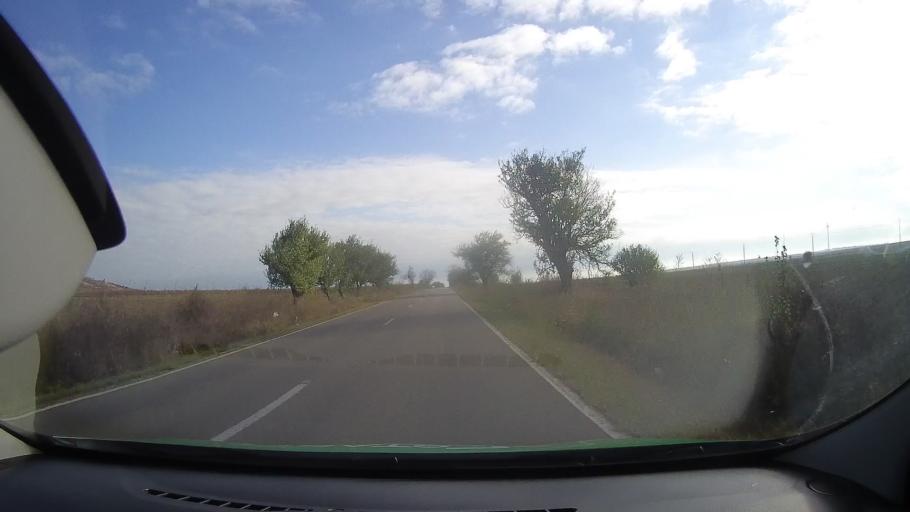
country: RO
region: Tulcea
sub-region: Comuna Mahmudia
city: Mahmudia
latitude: 45.0777
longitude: 29.0614
